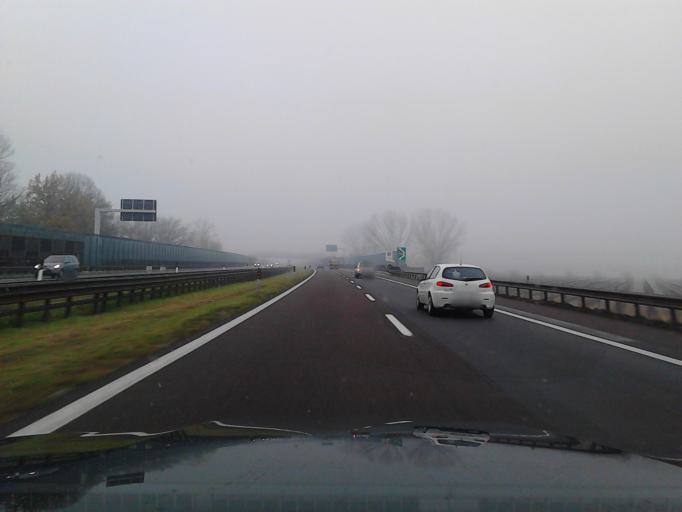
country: IT
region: Emilia-Romagna
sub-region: Provincia di Modena
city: Santa Croce Scuole
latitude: 44.7606
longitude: 10.8437
